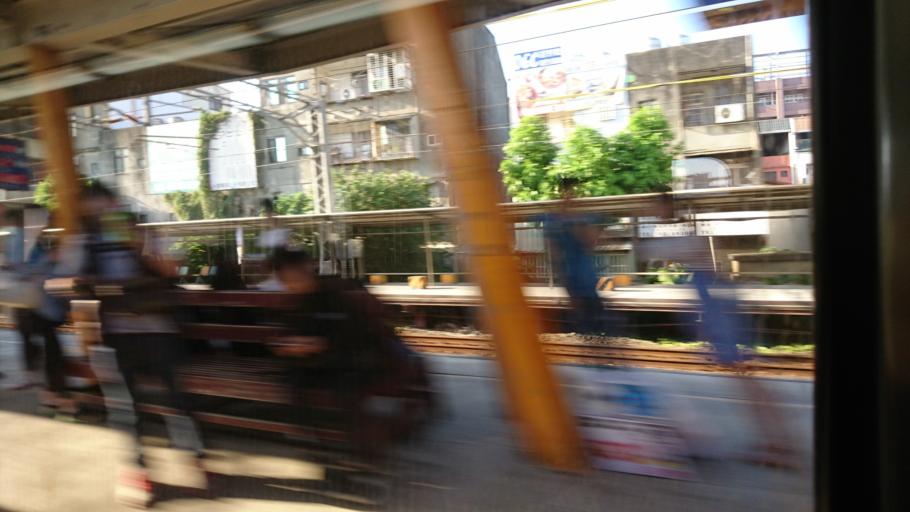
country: TW
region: Taiwan
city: Taoyuan City
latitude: 24.9724
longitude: 121.2583
